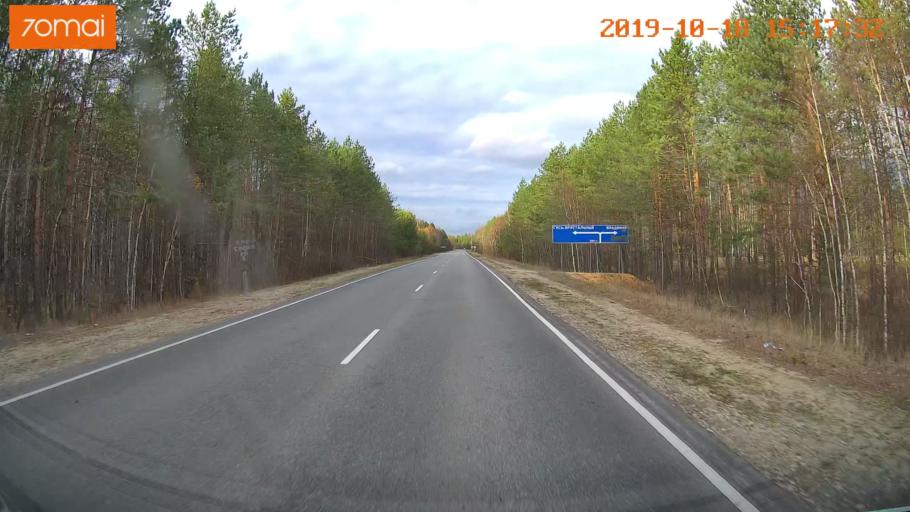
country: RU
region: Vladimir
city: Anopino
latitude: 55.6512
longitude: 40.7267
